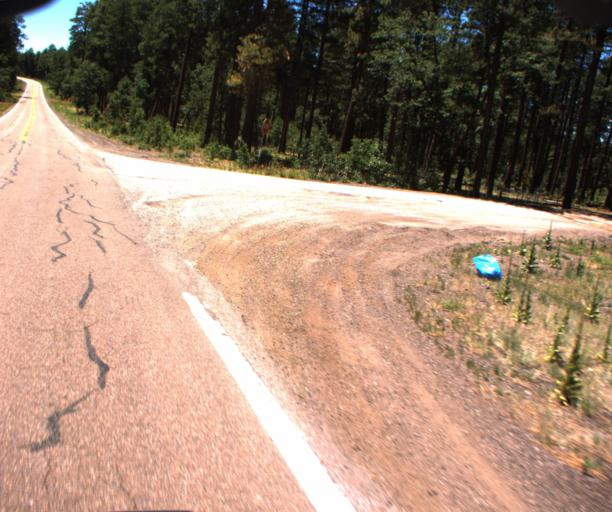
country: US
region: Arizona
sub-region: Gila County
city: Pine
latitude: 34.4562
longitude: -111.4115
